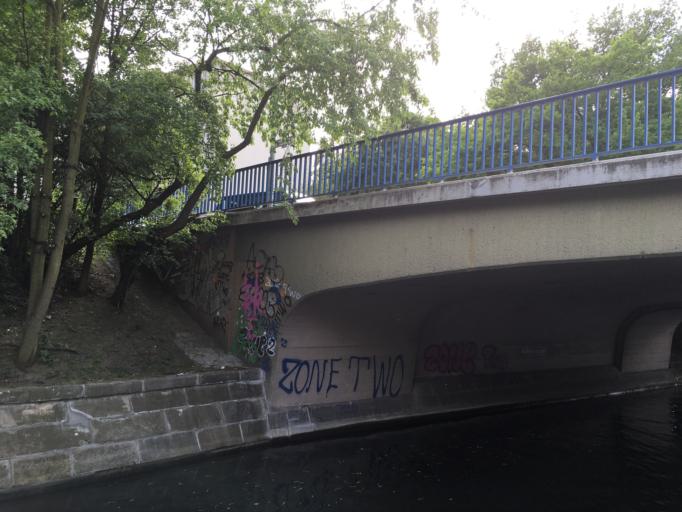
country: DE
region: Berlin
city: Bezirk Kreuzberg
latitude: 52.4973
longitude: 13.3990
